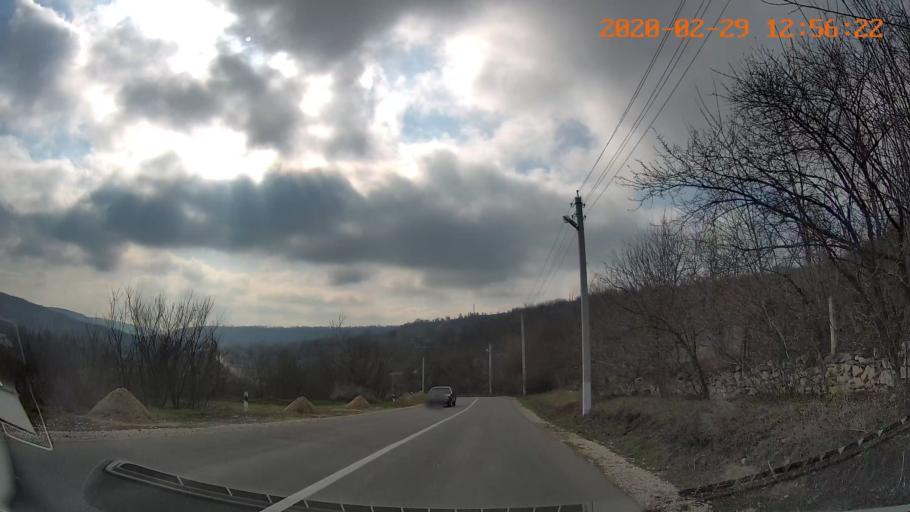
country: MD
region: Telenesti
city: Camenca
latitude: 48.0876
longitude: 28.7223
